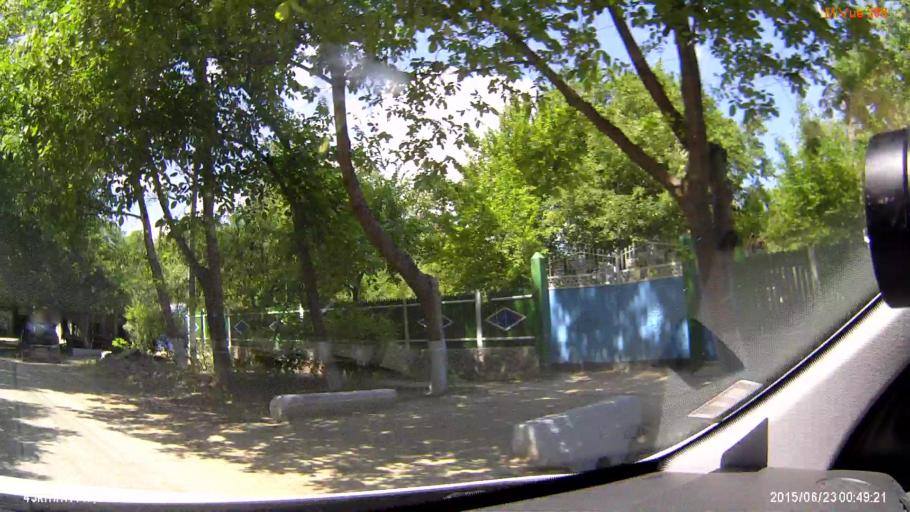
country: RO
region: Iasi
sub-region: Comuna Prisacani
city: Prisacani
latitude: 47.0702
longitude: 27.9551
